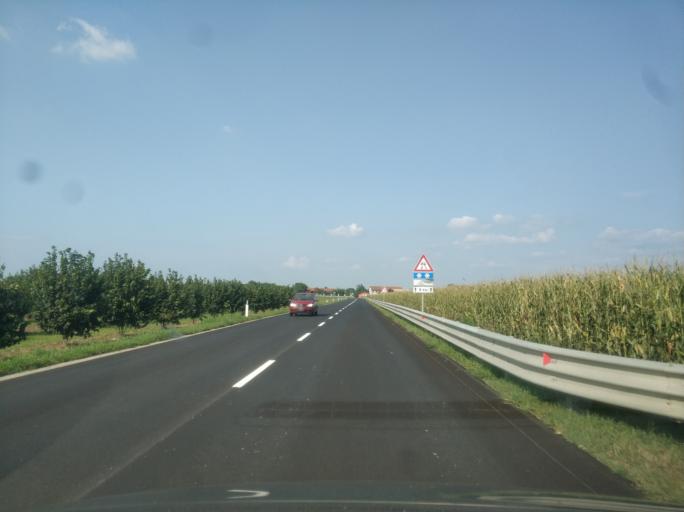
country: IT
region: Piedmont
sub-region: Provincia di Cuneo
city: Cervere
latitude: 44.6230
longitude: 7.7815
